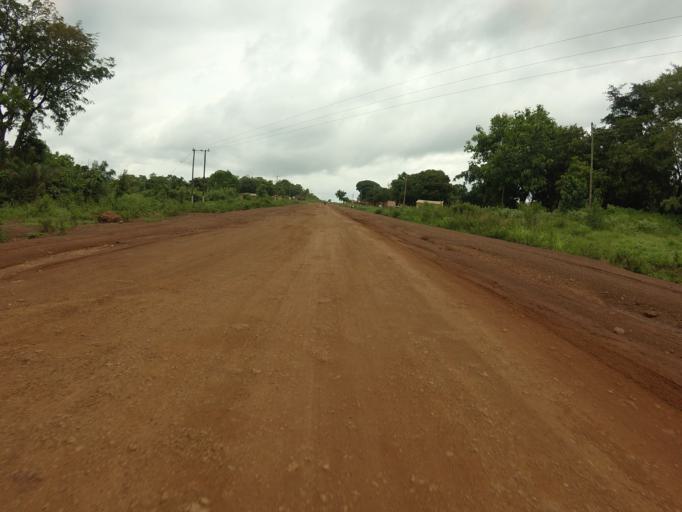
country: GH
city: Kpandae
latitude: 8.3139
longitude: 0.4805
